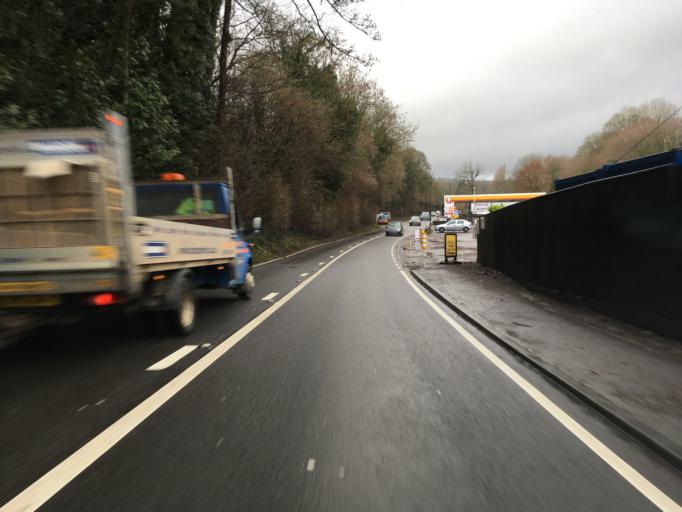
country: GB
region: England
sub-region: Gloucestershire
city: Nailsworth
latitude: 51.6991
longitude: -2.2227
